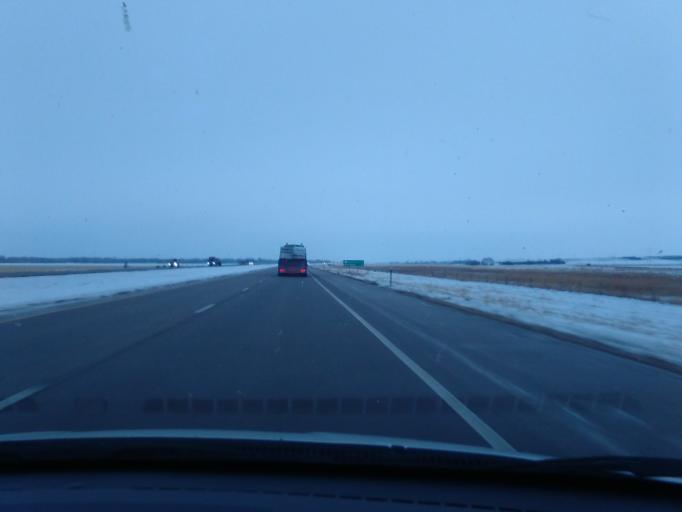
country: US
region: Nebraska
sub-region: Lincoln County
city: Sutherland
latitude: 41.1125
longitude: -101.3419
